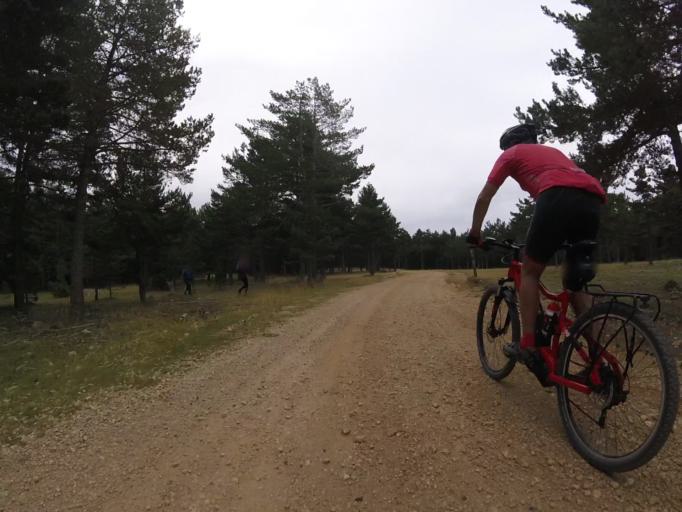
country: ES
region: Aragon
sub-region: Provincia de Teruel
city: Valdelinares
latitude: 40.3716
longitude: -0.6229
